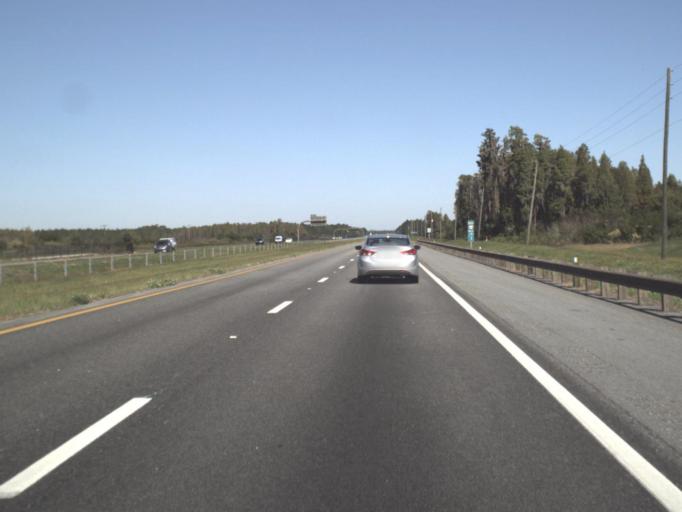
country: US
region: Florida
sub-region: Pasco County
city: Odessa
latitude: 28.1997
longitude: -82.5469
